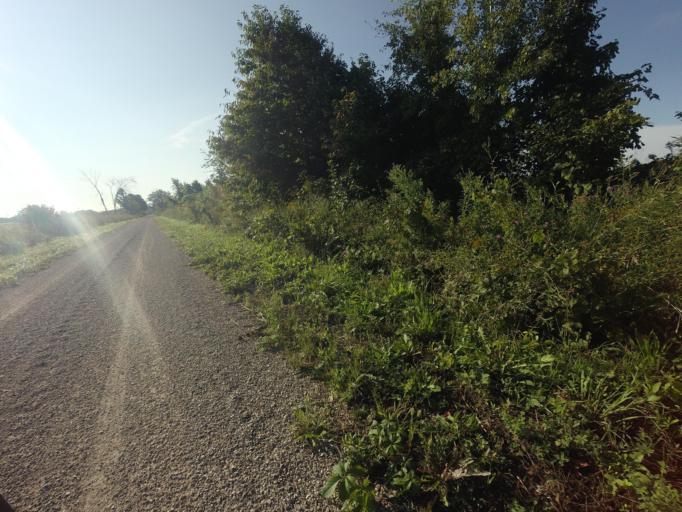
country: CA
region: Ontario
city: Goderich
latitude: 43.7551
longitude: -81.5118
